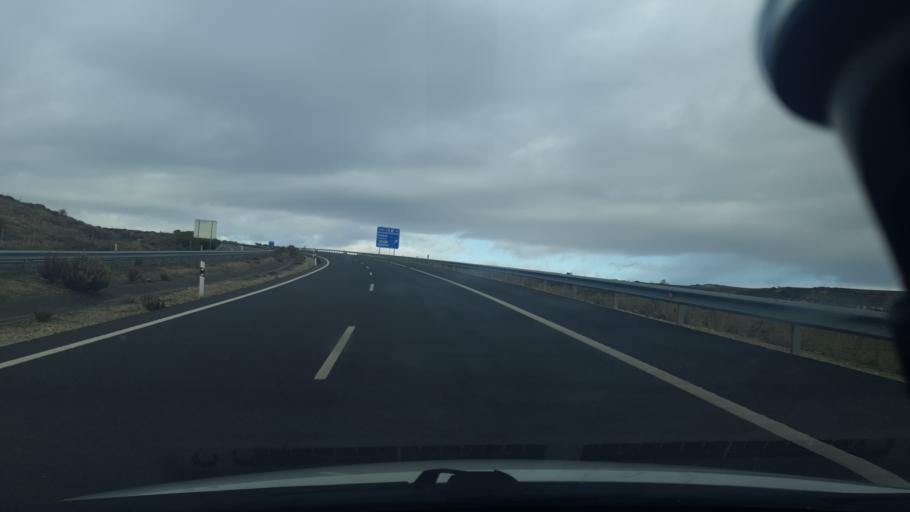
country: ES
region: Castille and Leon
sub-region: Provincia de Segovia
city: Cuellar
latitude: 41.3931
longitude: -4.2912
